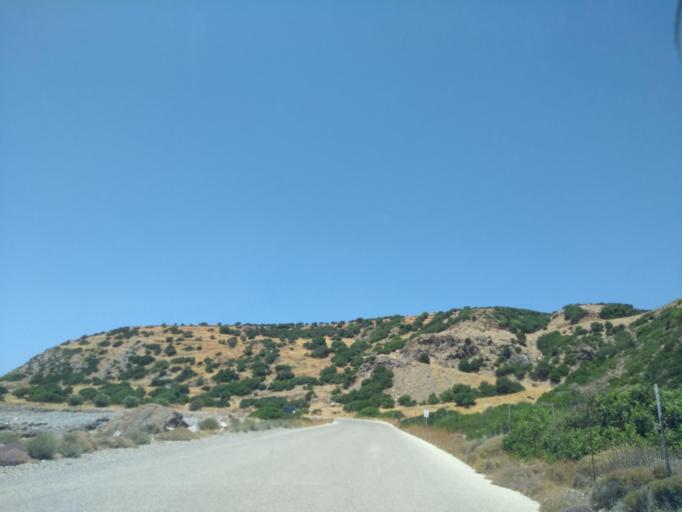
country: GR
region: Crete
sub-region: Nomos Chanias
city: Vryses
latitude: 35.3513
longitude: 23.5369
